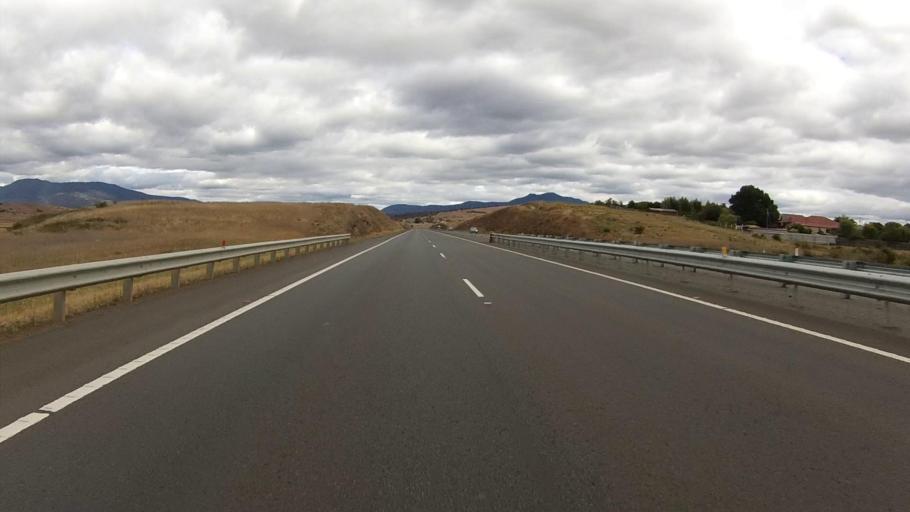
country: AU
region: Tasmania
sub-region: Brighton
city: Bridgewater
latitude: -42.7053
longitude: 147.2645
